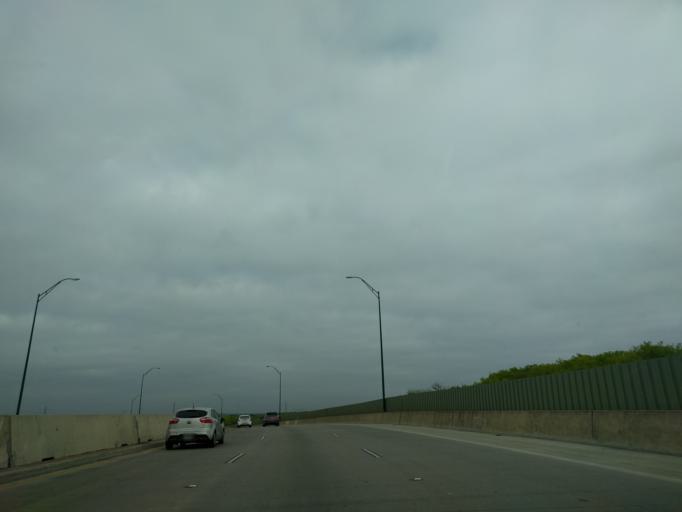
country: US
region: Texas
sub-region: Bexar County
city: Windcrest
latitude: 29.5436
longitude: -98.4264
